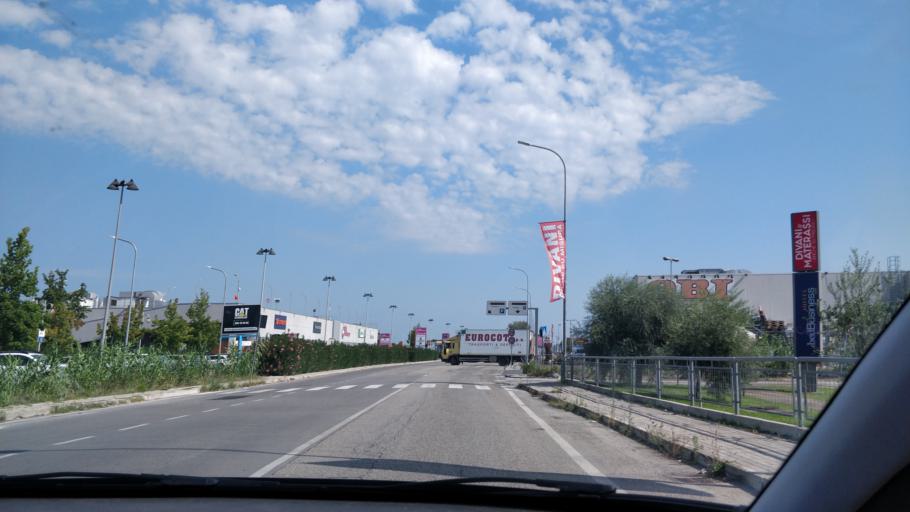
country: IT
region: Abruzzo
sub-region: Provincia di Pescara
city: Santa Teresa
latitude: 42.4137
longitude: 14.1690
